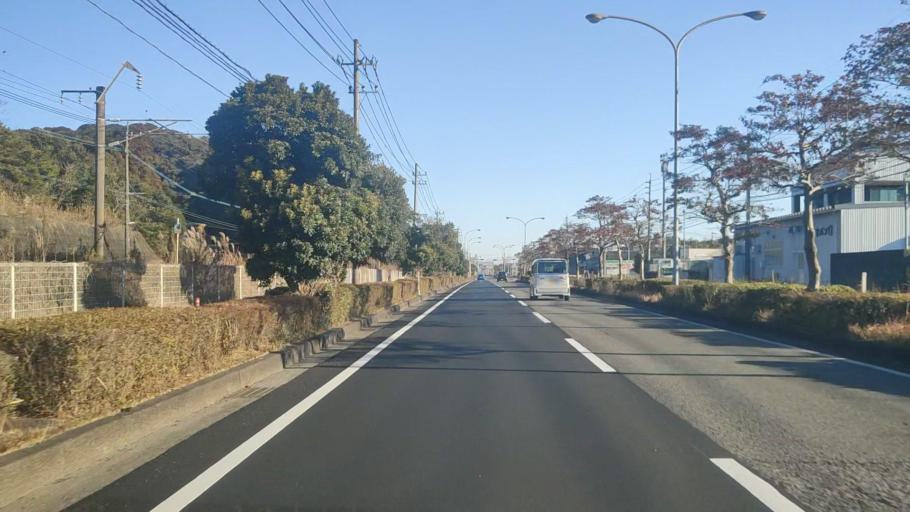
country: JP
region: Miyazaki
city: Nobeoka
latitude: 32.4521
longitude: 131.6410
